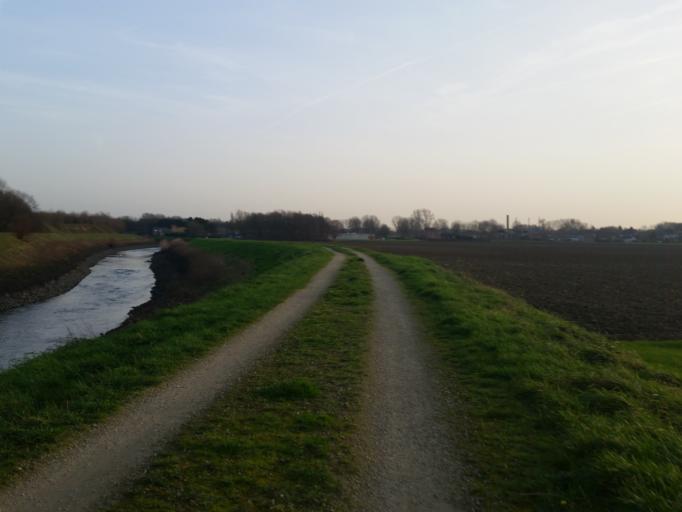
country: BE
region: Flanders
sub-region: Provincie Vlaams-Brabant
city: Zemst
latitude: 50.9930
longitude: 4.4652
